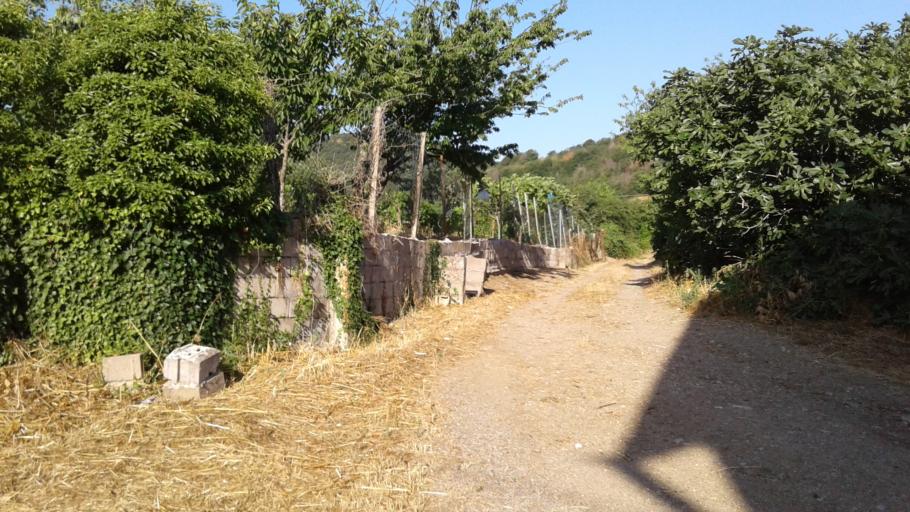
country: IT
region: Sardinia
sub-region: Provincia di Olbia-Tempio
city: Tempio Pausania
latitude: 40.9082
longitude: 9.0860
